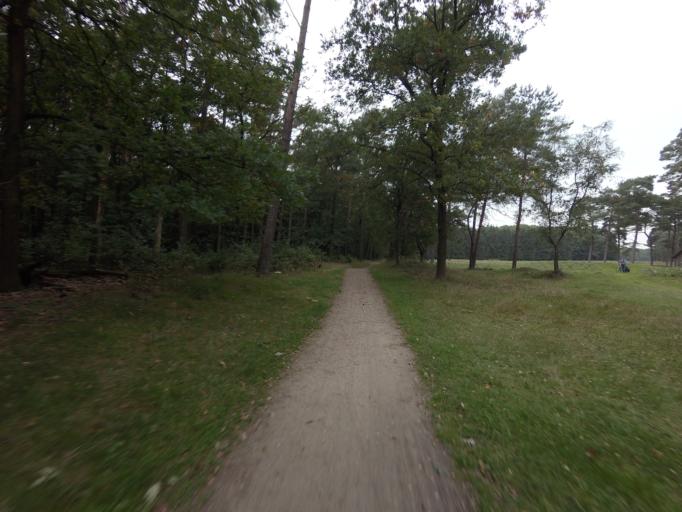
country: NL
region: North Holland
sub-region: Gemeente Hilversum
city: Hilversum
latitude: 52.1954
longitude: 5.1925
